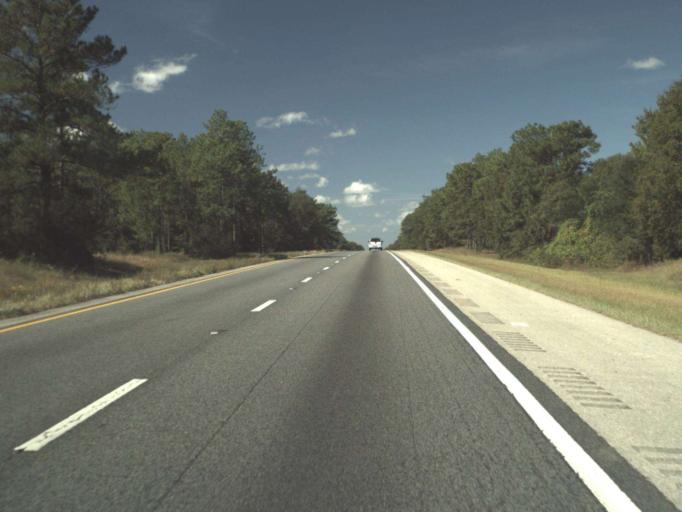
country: US
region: Florida
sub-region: Washington County
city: Chipley
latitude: 30.7460
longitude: -85.4856
